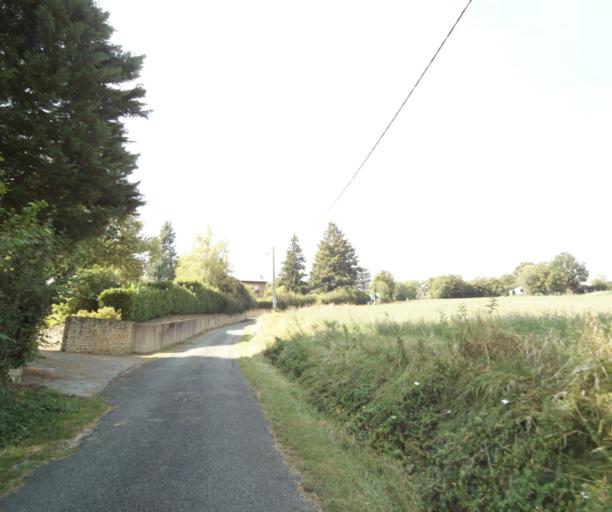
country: FR
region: Bourgogne
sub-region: Departement de Saone-et-Loire
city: Tournus
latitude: 46.5722
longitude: 4.8912
